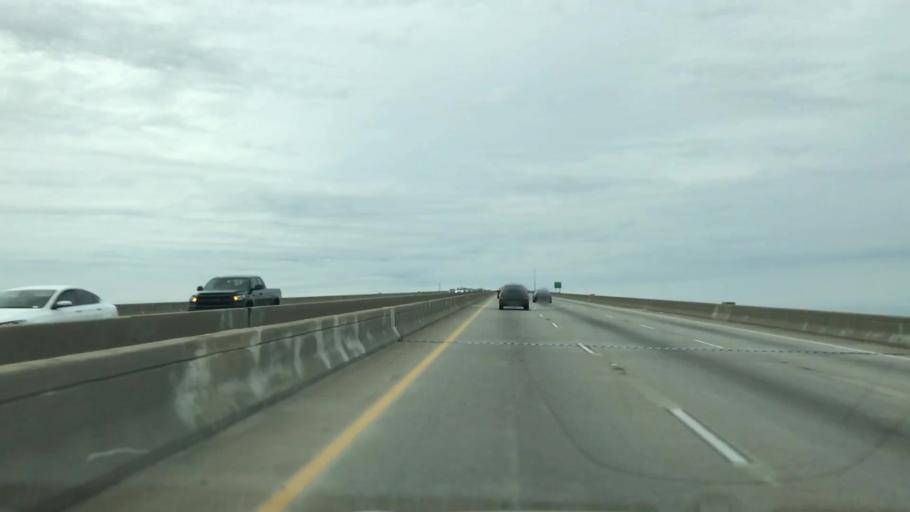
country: US
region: South Carolina
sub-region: Charleston County
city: Mount Pleasant
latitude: 32.8562
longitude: -79.8904
